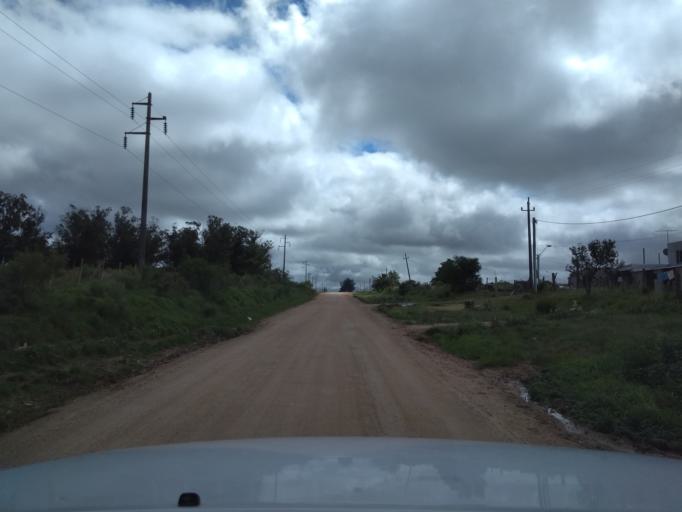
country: UY
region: Canelones
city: Pando
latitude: -34.6960
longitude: -55.9728
